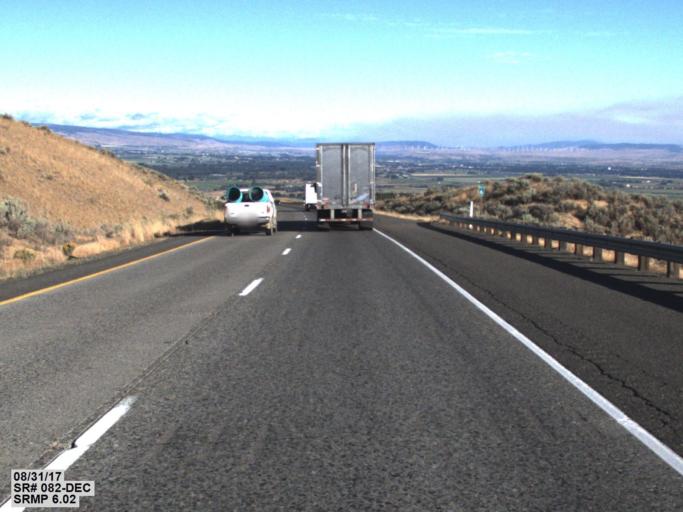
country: US
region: Washington
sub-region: Kittitas County
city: Kittitas
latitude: 46.9017
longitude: -120.4527
